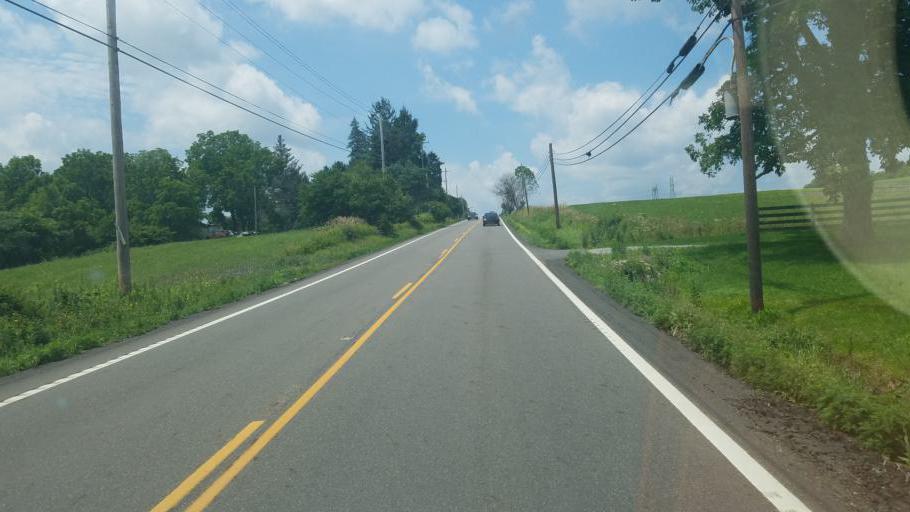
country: US
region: Ohio
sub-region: Columbiana County
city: Lisbon
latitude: 40.7700
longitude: -80.7967
